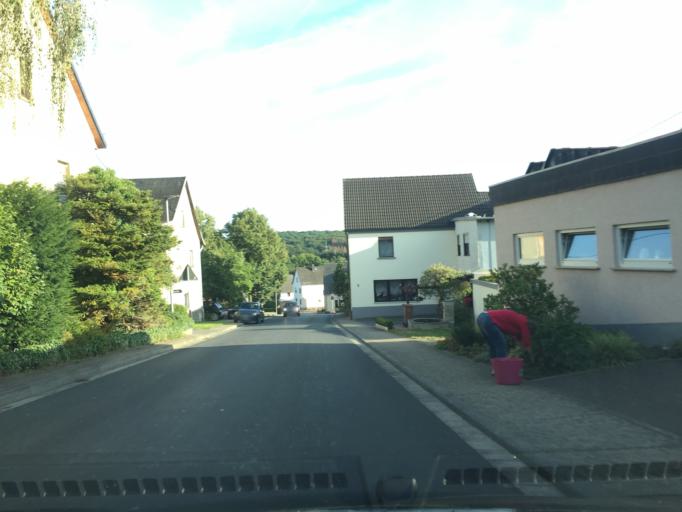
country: DE
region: Rheinland-Pfalz
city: Ruppach-Goldhausen
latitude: 50.4625
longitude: 7.8807
